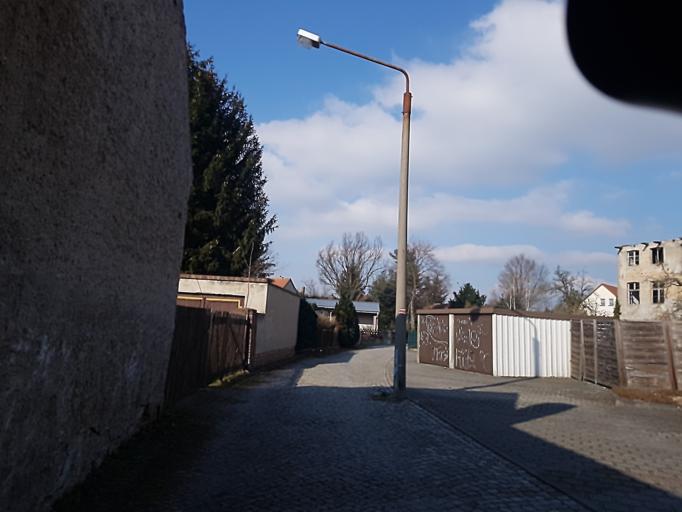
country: DE
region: Brandenburg
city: Doberlug-Kirchhain
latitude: 51.6357
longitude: 13.5606
